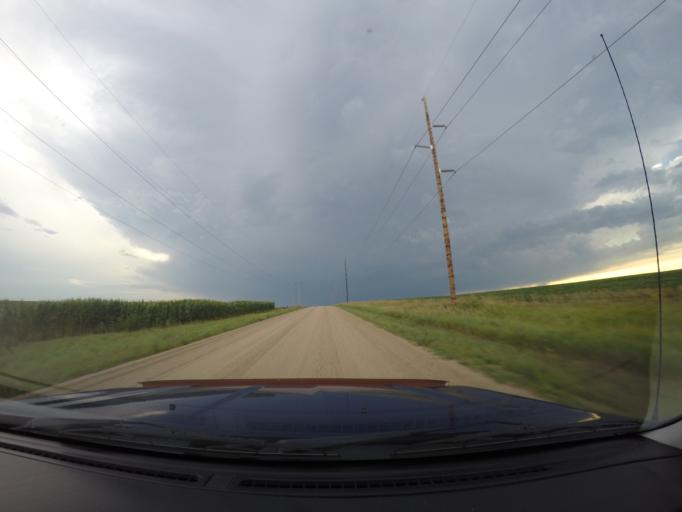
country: US
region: Nebraska
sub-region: Buffalo County
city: Kearney
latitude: 40.8445
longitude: -99.0993
